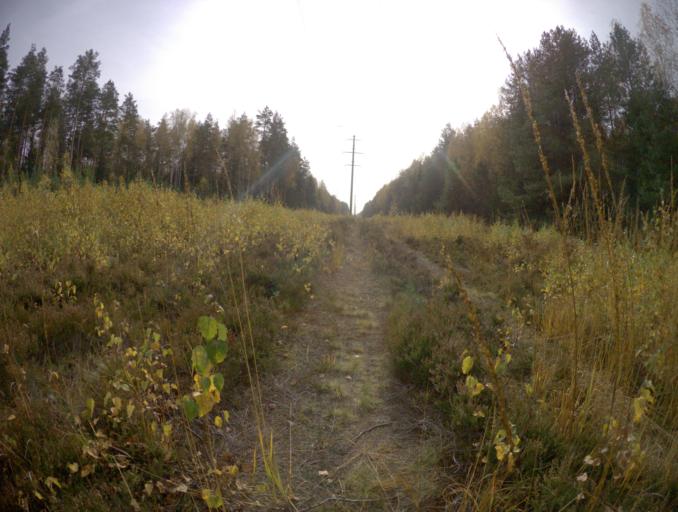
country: RU
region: Vladimir
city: Vorsha
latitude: 55.9628
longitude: 40.1456
